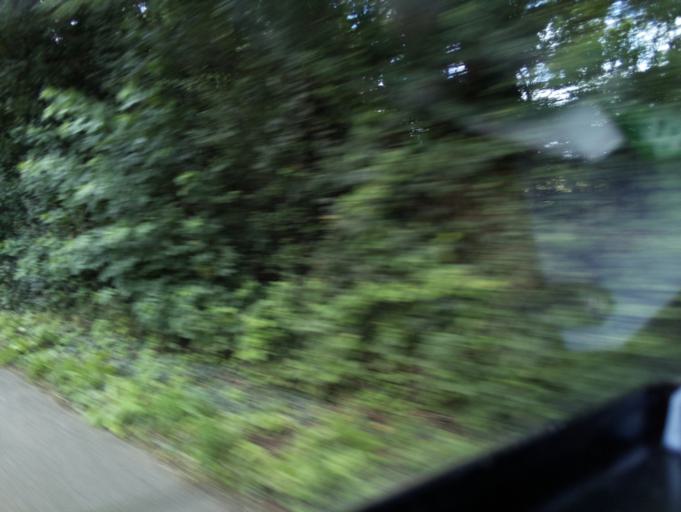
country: GB
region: England
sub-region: Nottinghamshire
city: Ruddington
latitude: 52.8539
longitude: -1.1044
